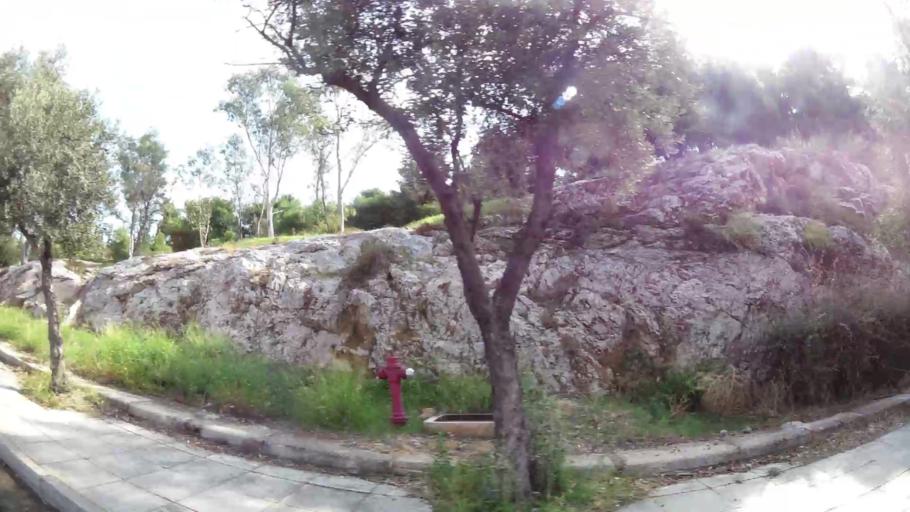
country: GR
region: Attica
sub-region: Nomarchia Athinas
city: Athens
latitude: 37.9708
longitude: 23.7157
